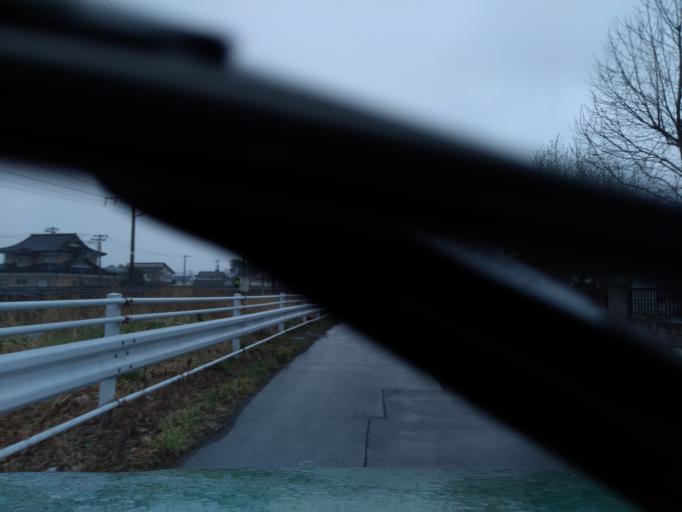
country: JP
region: Iwate
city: Ichinoseki
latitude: 38.9404
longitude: 141.1361
